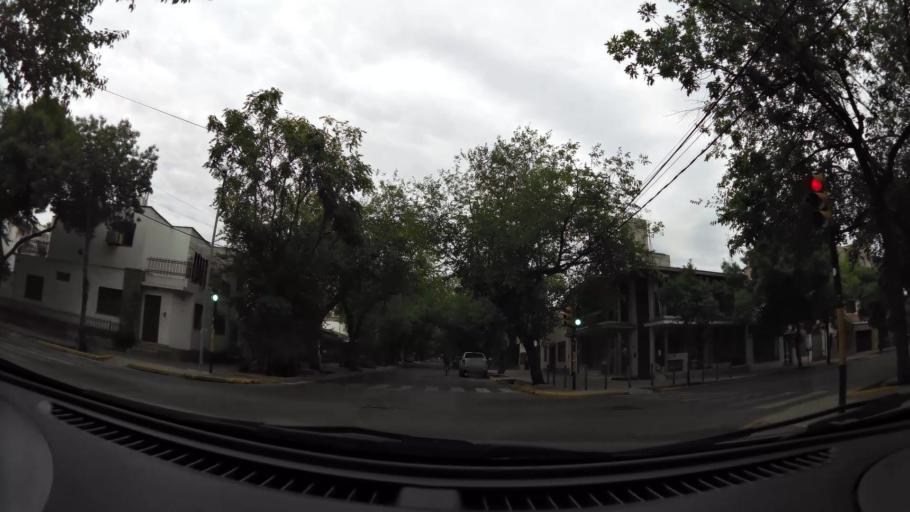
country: AR
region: Mendoza
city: Mendoza
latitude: -32.9009
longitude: -68.8487
